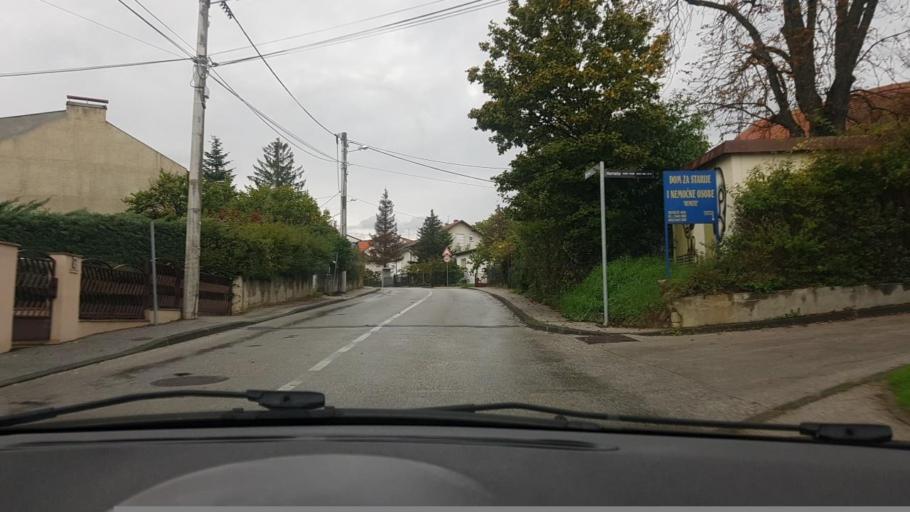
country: HR
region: Grad Zagreb
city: Zagreb
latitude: 45.8422
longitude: 15.9957
